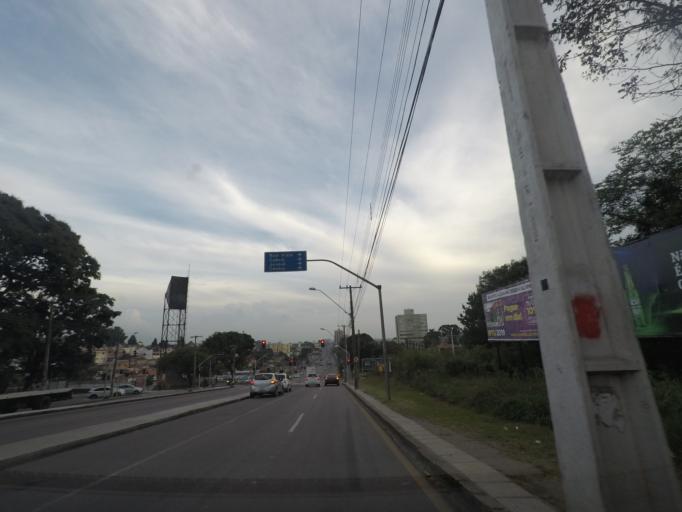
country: BR
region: Parana
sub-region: Curitiba
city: Curitiba
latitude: -25.3762
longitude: -49.2247
